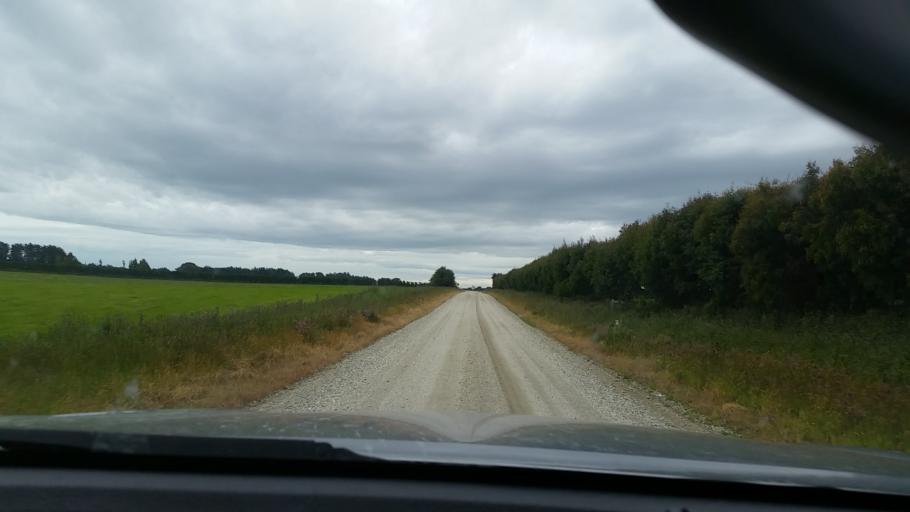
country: NZ
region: Southland
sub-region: Gore District
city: Gore
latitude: -46.2742
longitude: 168.7181
